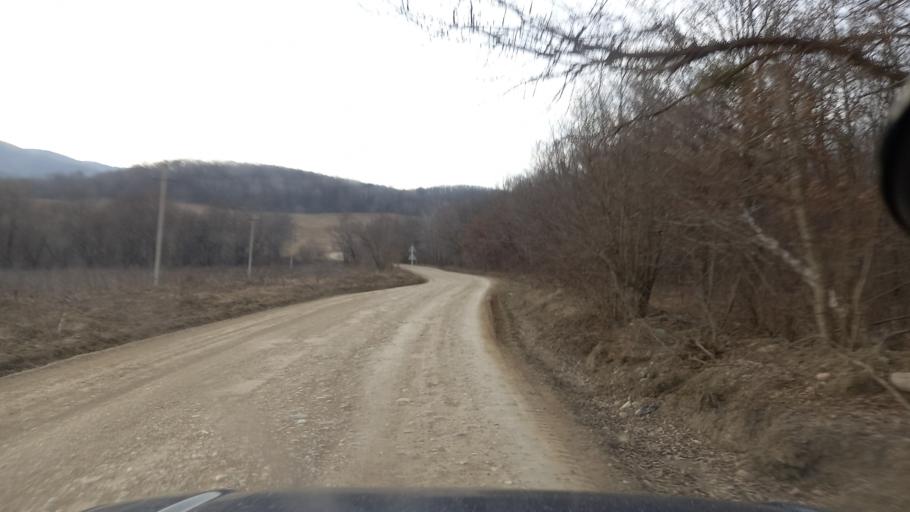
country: RU
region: Adygeya
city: Kamennomostskiy
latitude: 44.1452
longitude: 40.2561
